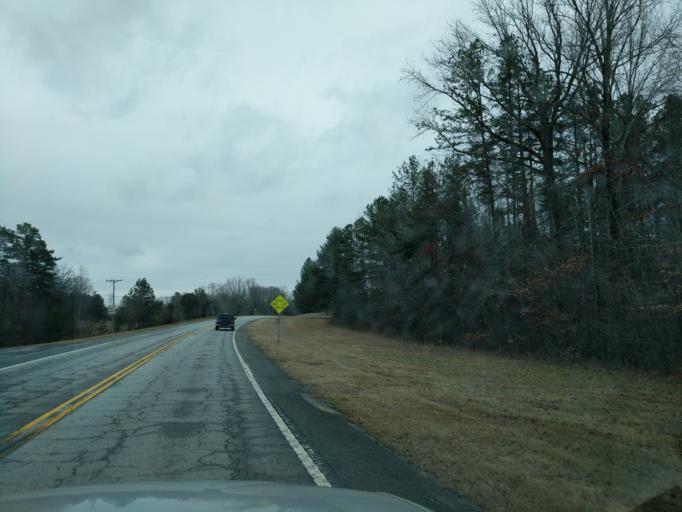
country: US
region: South Carolina
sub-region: Oconee County
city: Walhalla
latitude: 34.8528
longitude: -83.0328
